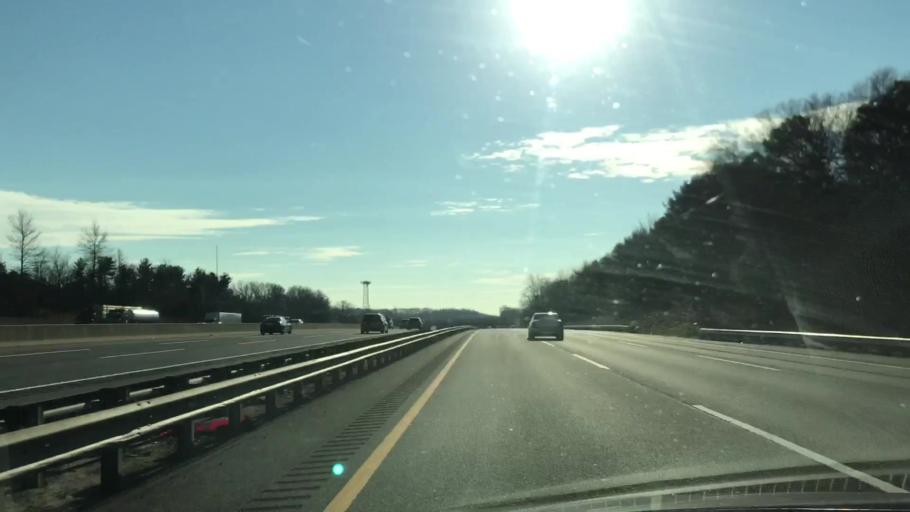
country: US
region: New Jersey
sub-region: Middlesex County
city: Milltown
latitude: 40.4522
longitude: -74.4219
